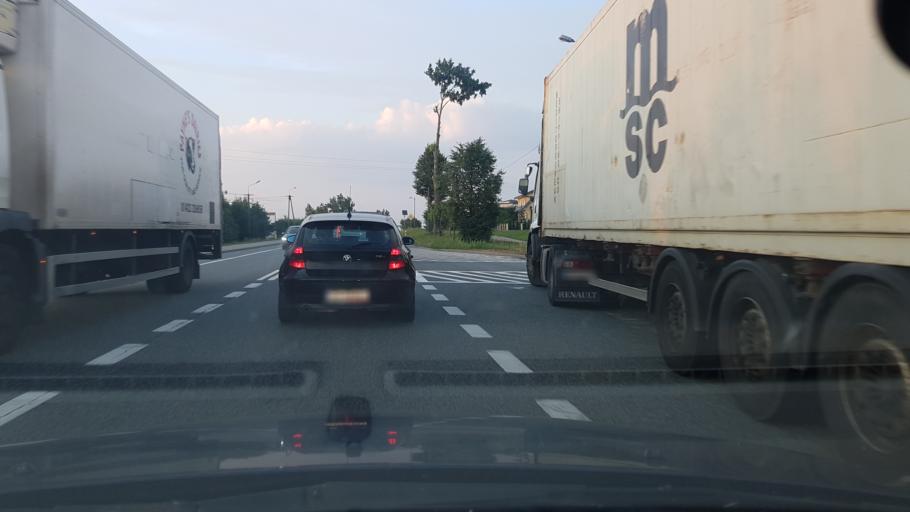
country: PL
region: Masovian Voivodeship
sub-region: Powiat mlawski
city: Mlawa
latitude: 53.1657
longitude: 20.4149
